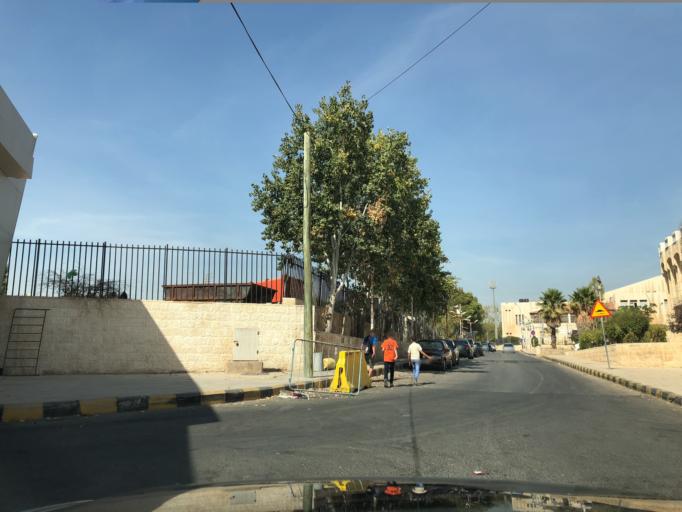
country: JO
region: Amman
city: Amman
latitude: 31.9795
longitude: 35.9071
